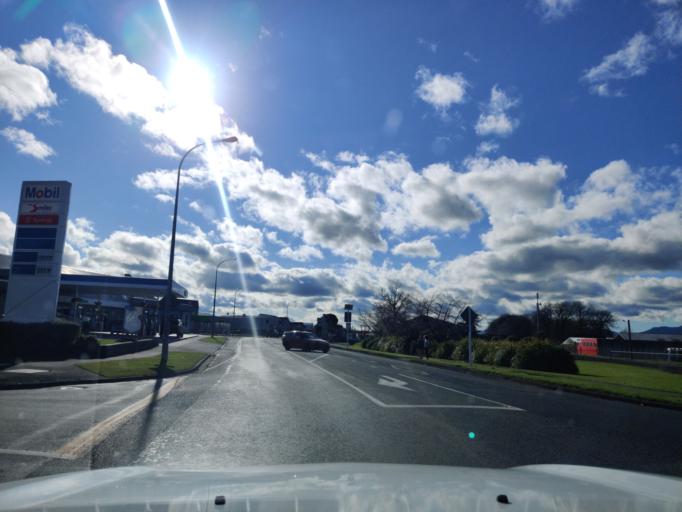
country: NZ
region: Waikato
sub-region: Matamata-Piako District
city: Matamata
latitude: -37.8147
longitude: 175.7710
